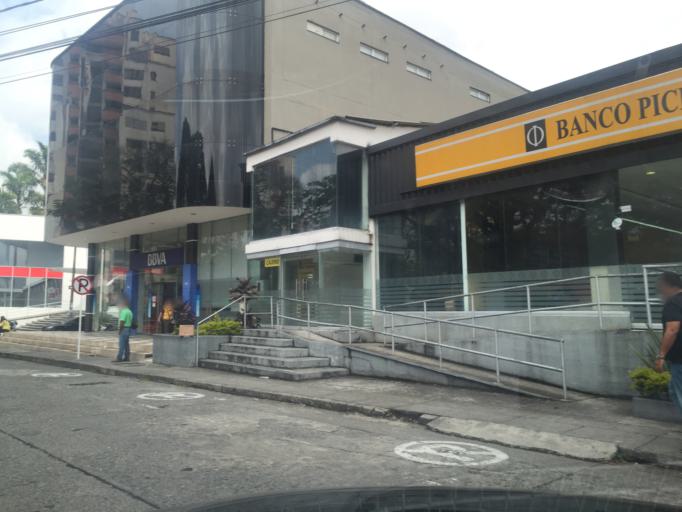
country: CO
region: Risaralda
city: Pereira
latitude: 4.8082
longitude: -75.6805
